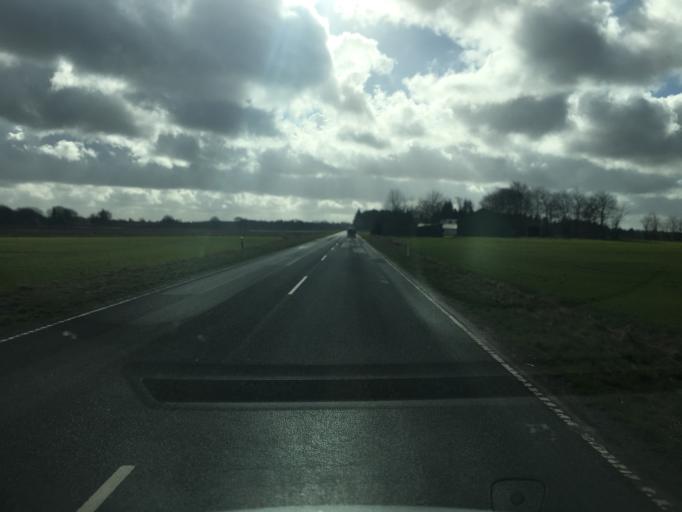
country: DK
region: South Denmark
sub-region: Aabenraa Kommune
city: Krusa
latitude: 54.9049
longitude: 9.3726
